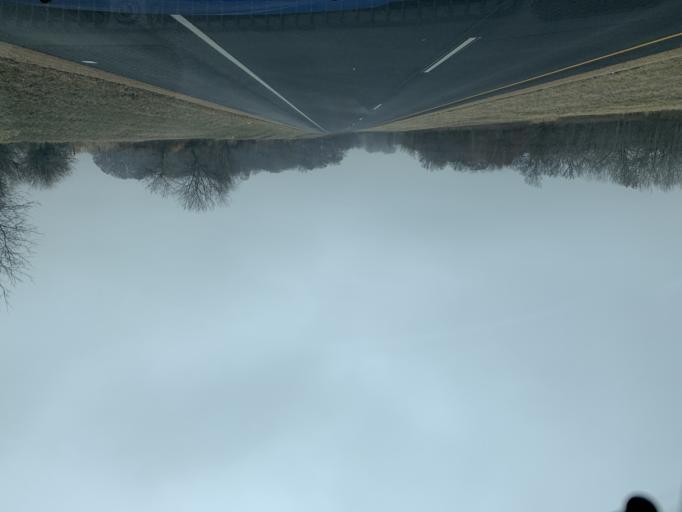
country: US
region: Wisconsin
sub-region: Dane County
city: Sun Prairie
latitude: 43.2288
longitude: -89.1567
